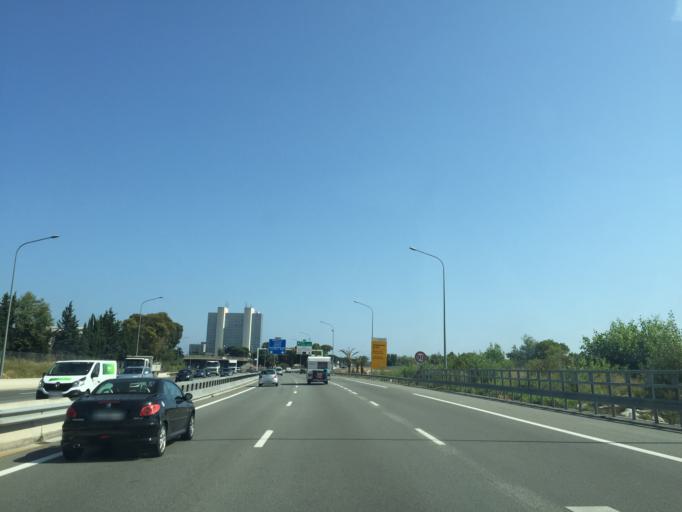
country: FR
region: Provence-Alpes-Cote d'Azur
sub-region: Departement des Alpes-Maritimes
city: Saint-Laurent-du-Var
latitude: 43.6783
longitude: 7.1942
